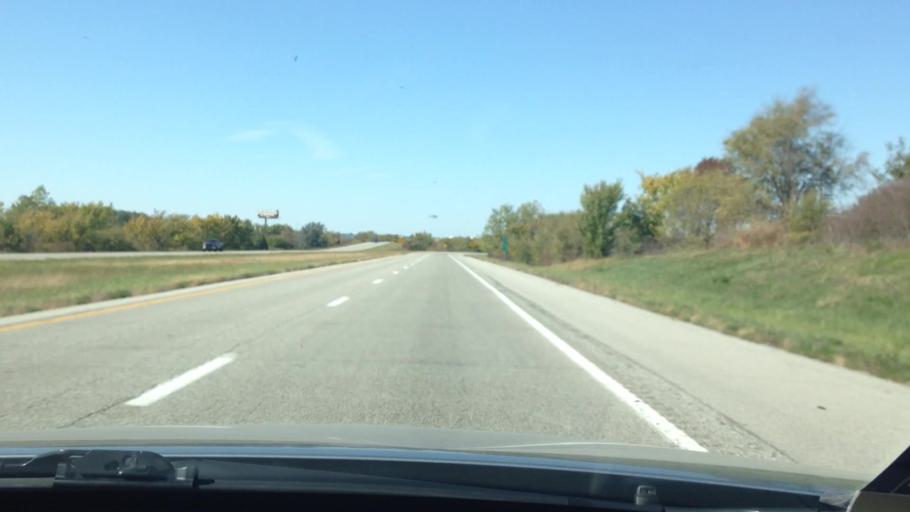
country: US
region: Missouri
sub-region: Platte County
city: Weatherby Lake
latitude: 39.3175
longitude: -94.6871
